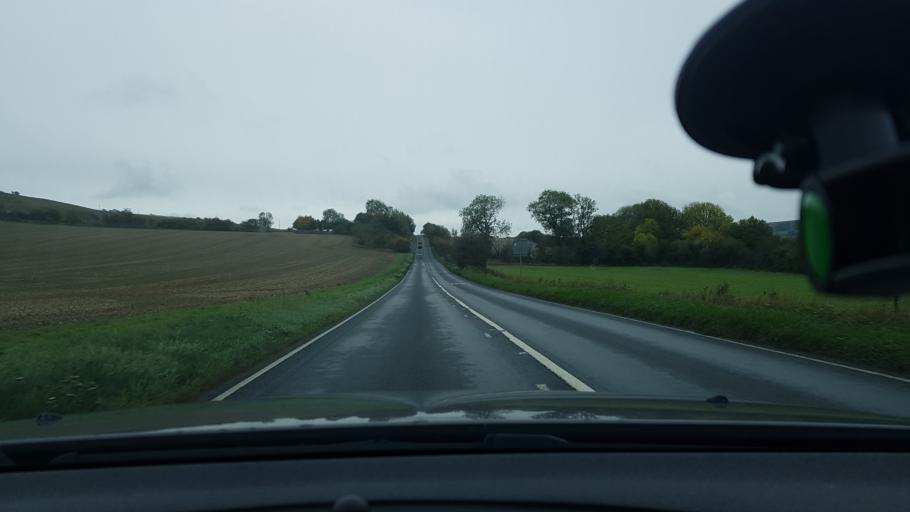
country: GB
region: England
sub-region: Borough of Swindon
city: Chiseldon
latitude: 51.4904
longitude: -1.7163
